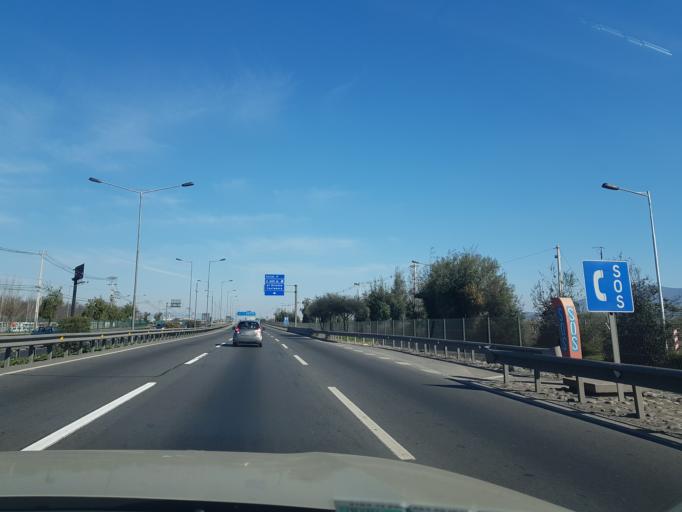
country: CL
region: Santiago Metropolitan
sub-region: Provincia de Santiago
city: Lo Prado
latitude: -33.4104
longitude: -70.7825
